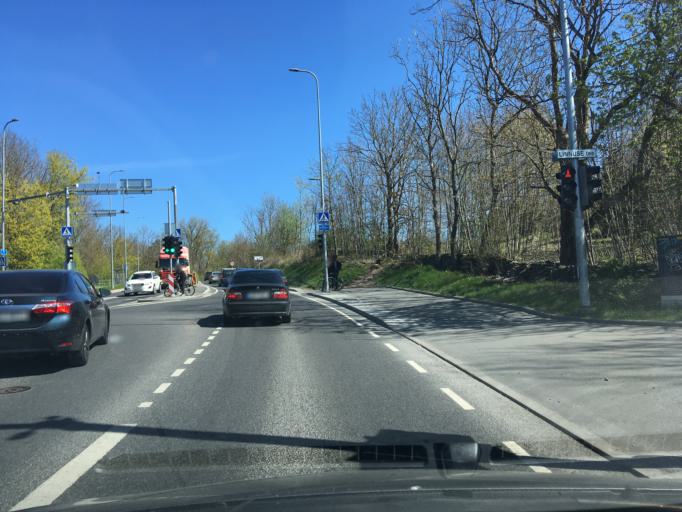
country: EE
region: Harju
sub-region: Tallinna linn
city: Kose
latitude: 59.4601
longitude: 24.9046
